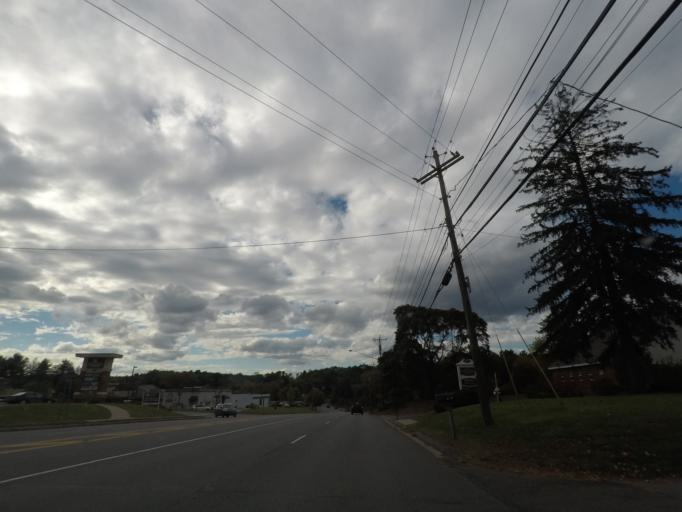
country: US
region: New York
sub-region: Albany County
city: Westmere
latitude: 42.6983
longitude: -73.8904
